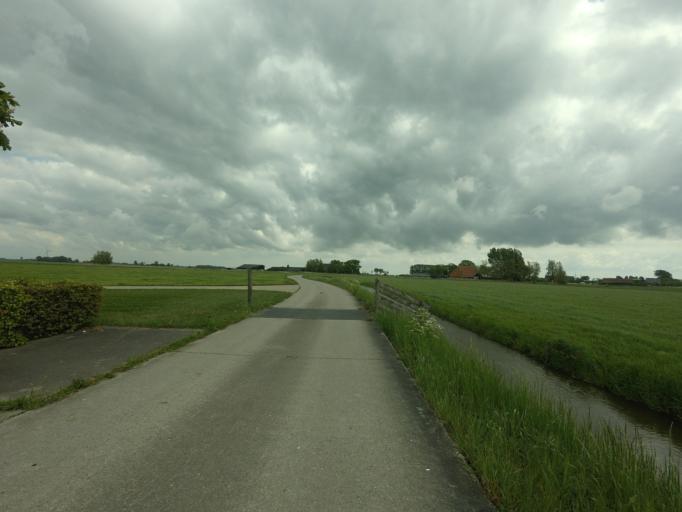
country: NL
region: Friesland
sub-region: Gemeente Littenseradiel
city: Wommels
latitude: 53.1075
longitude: 5.6187
